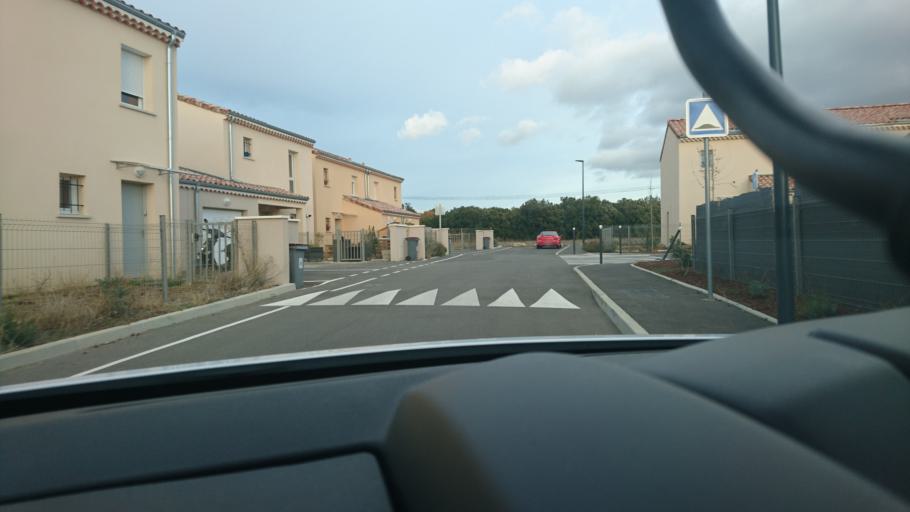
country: FR
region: Provence-Alpes-Cote d'Azur
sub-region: Departement du Vaucluse
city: Bollene
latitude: 44.2846
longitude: 4.7670
